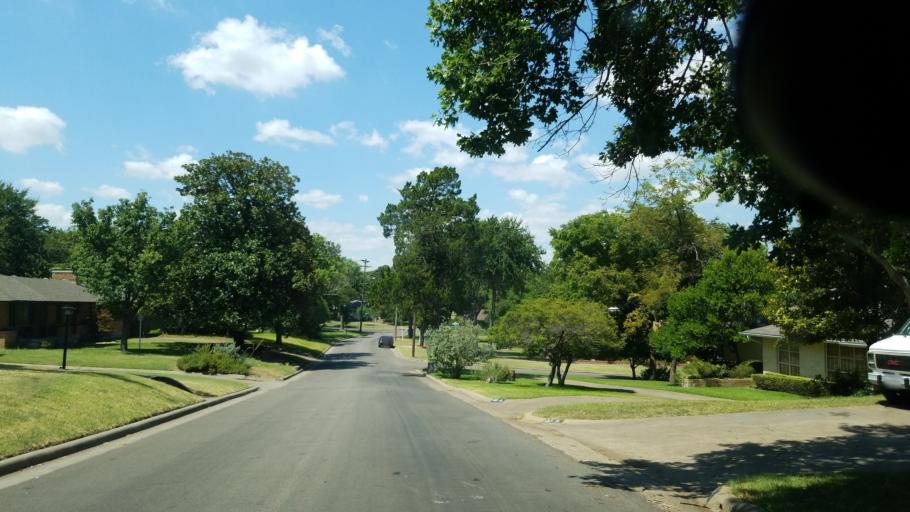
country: US
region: Texas
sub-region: Dallas County
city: Cockrell Hill
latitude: 32.7313
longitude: -96.8349
